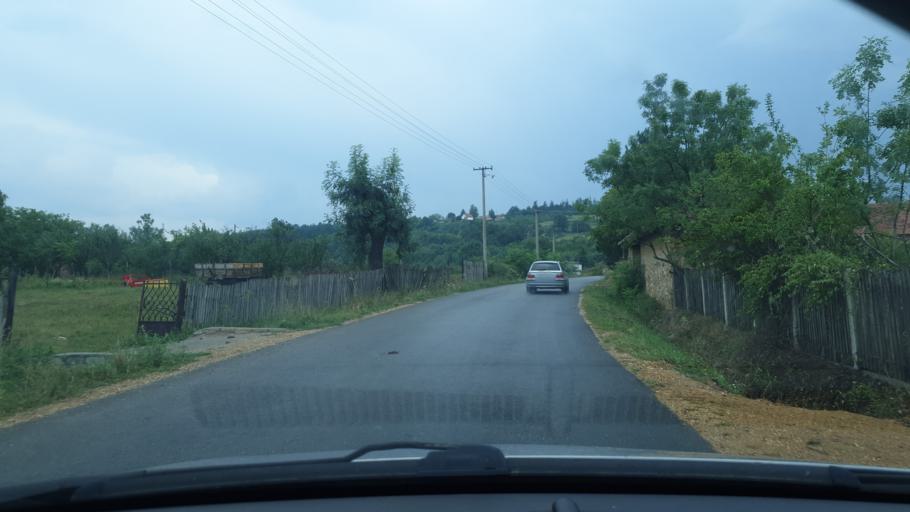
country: RS
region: Central Serbia
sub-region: Sumadijski Okrug
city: Kragujevac
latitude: 44.0636
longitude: 20.7902
